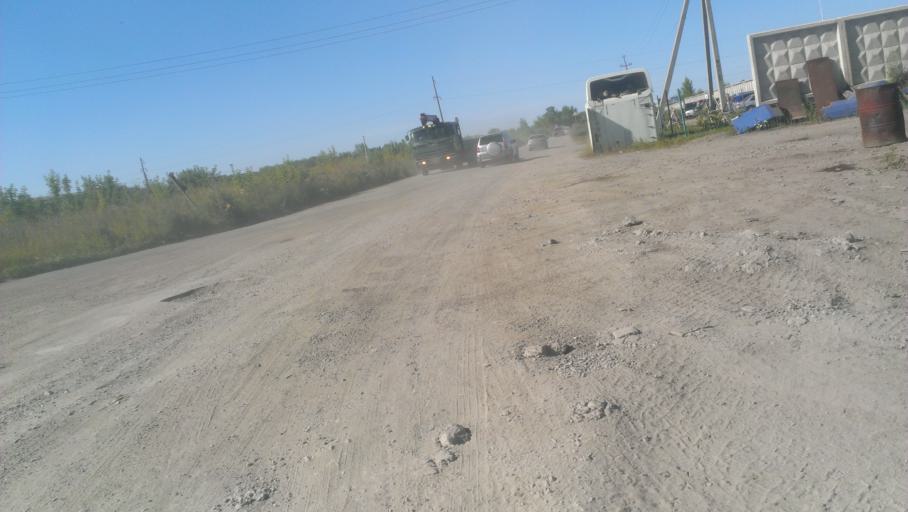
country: RU
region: Altai Krai
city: Novosilikatnyy
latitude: 53.3347
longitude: 83.6353
